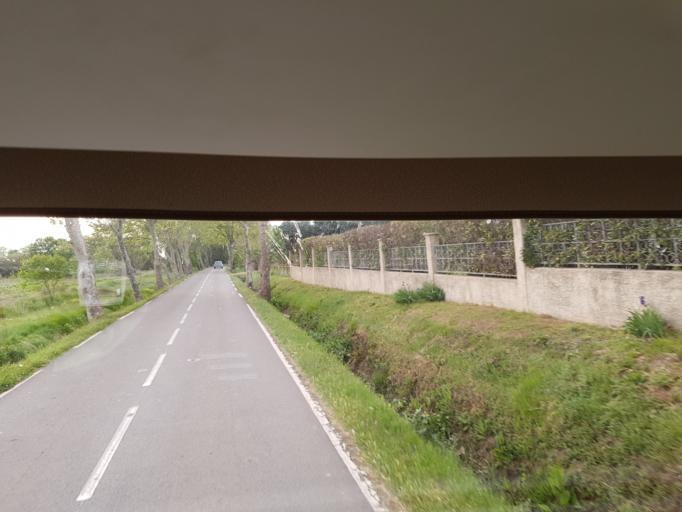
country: FR
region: Languedoc-Roussillon
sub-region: Departement de l'Herault
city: Florensac
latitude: 43.3788
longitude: 3.4738
